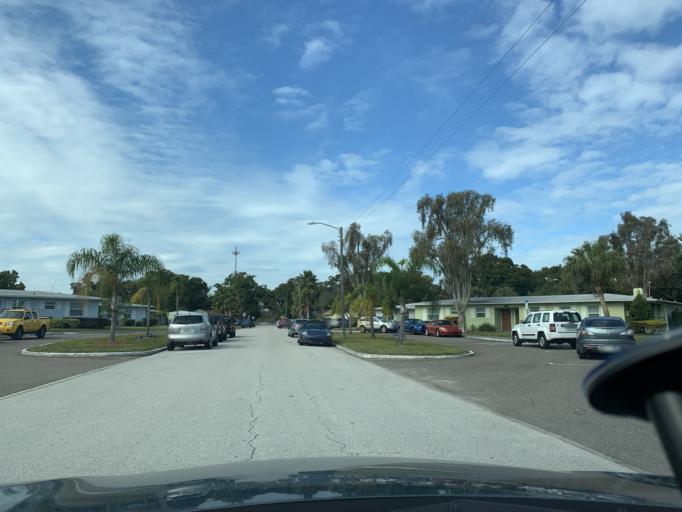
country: US
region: Florida
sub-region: Pinellas County
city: Saint Petersburg
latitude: 27.7893
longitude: -82.6573
